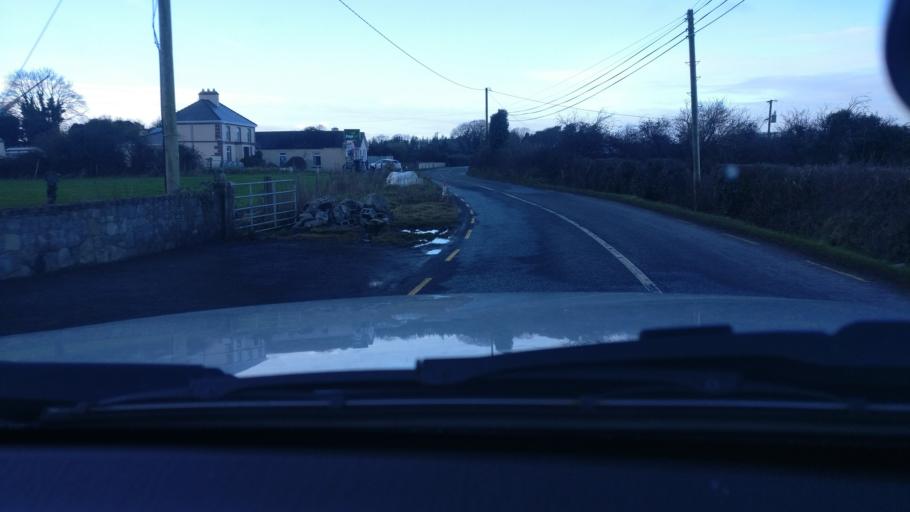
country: IE
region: Connaught
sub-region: County Galway
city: Loughrea
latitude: 53.2249
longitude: -8.4043
